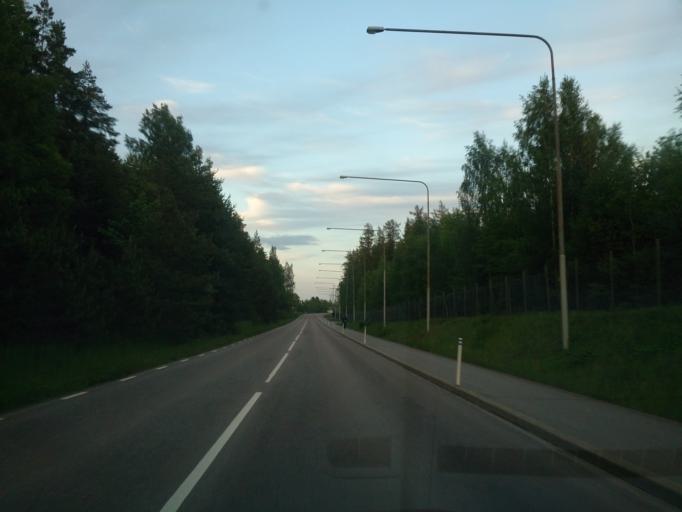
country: SE
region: OEstergoetland
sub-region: Linkopings Kommun
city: Malmslatt
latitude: 58.4094
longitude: 15.5414
